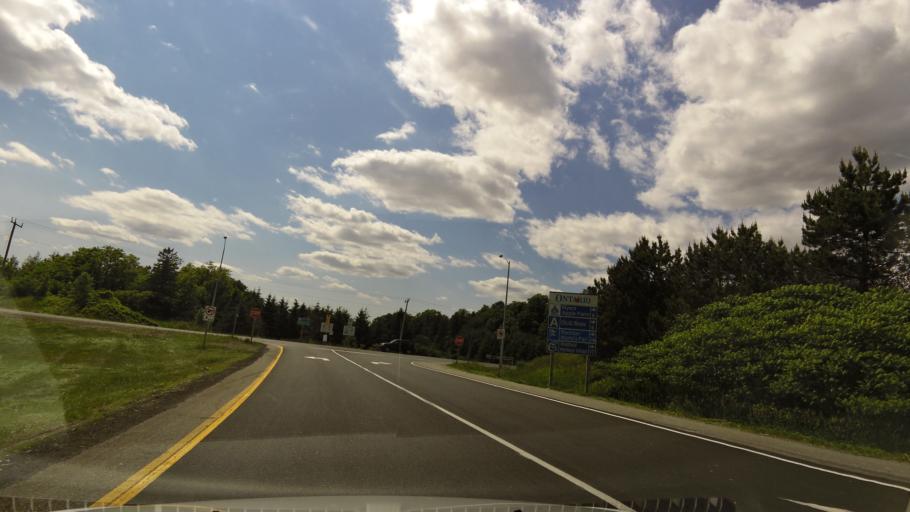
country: CA
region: Ontario
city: Ancaster
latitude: 43.2028
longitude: -80.0446
